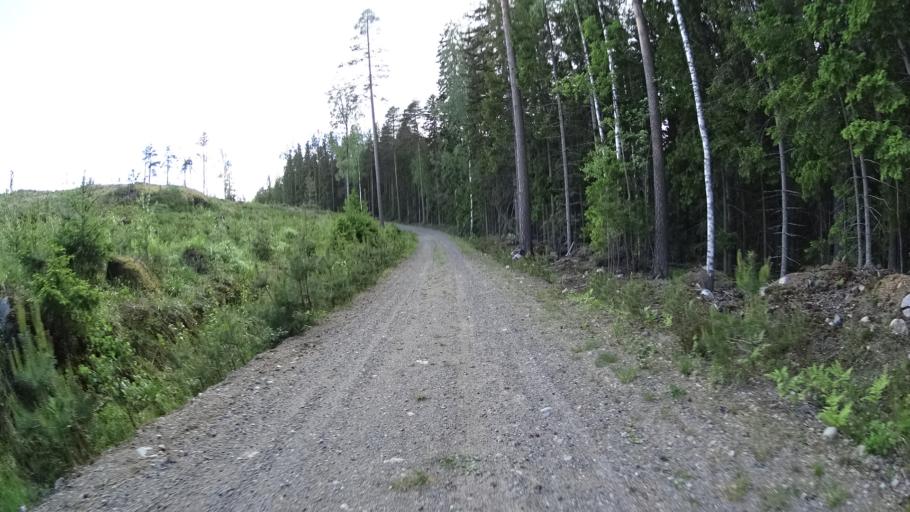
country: FI
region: Varsinais-Suomi
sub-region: Salo
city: Kisko
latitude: 60.1915
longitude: 23.5550
